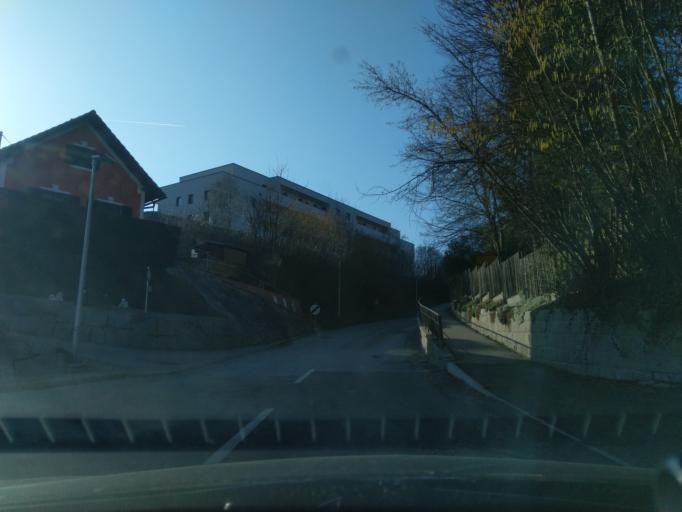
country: DE
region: Bavaria
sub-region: Lower Bavaria
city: Bad Fussing
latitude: 48.3227
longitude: 13.3382
